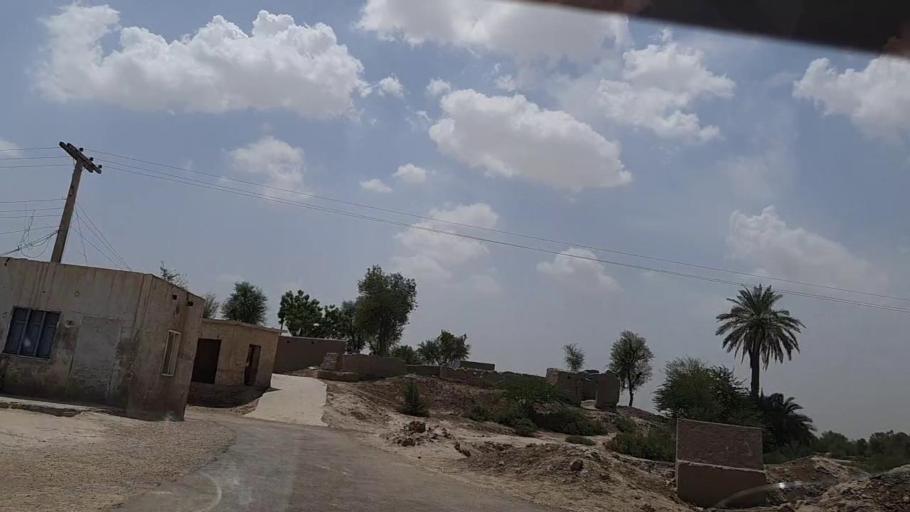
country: PK
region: Sindh
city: Bhan
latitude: 26.5419
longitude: 67.6353
